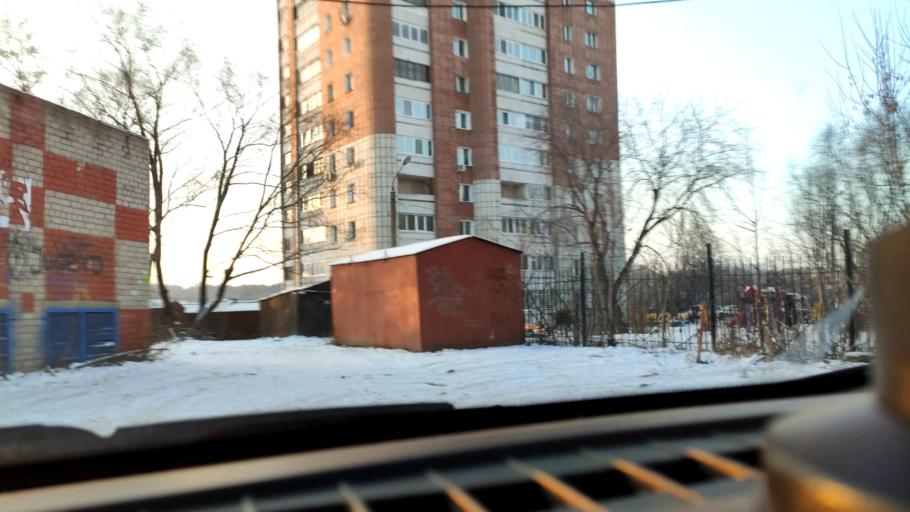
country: RU
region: Perm
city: Perm
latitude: 57.9632
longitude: 56.2132
